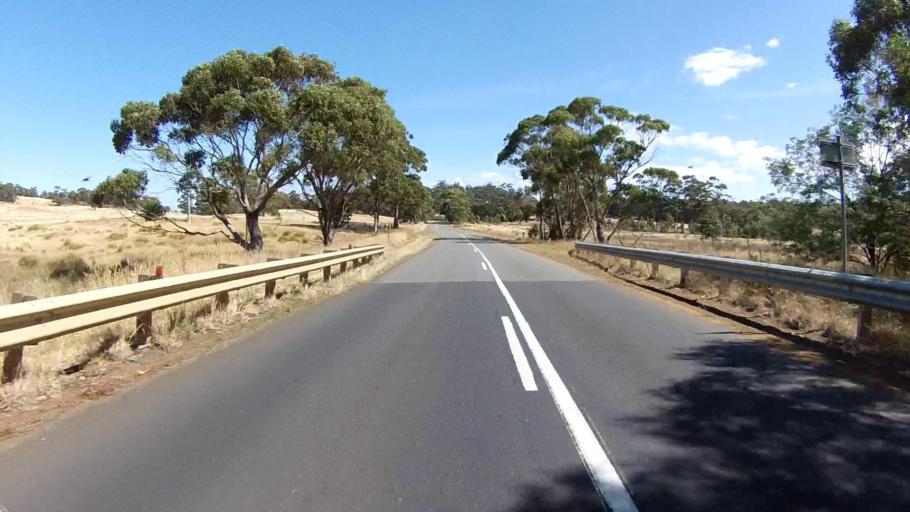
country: AU
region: Tasmania
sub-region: Sorell
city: Sorell
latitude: -42.3053
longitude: 147.9669
